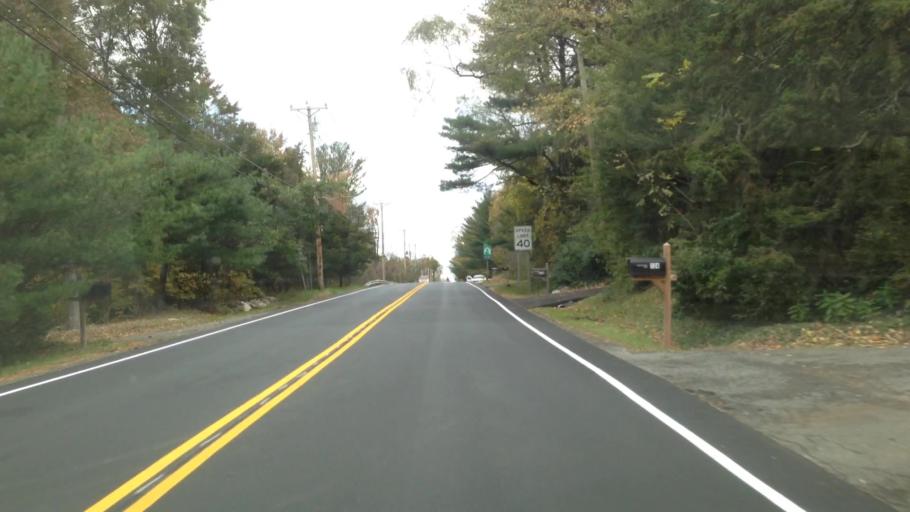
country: US
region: New York
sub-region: Ulster County
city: New Paltz
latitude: 41.7370
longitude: -74.0914
